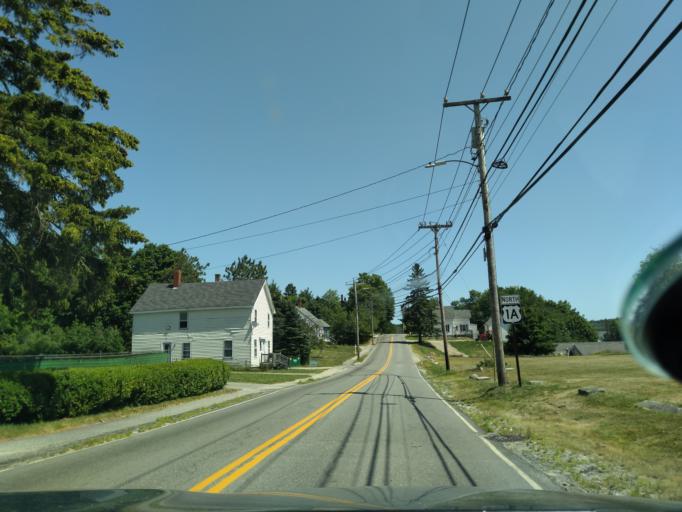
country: US
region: Maine
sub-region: Washington County
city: Machias
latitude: 44.7162
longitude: -67.4581
